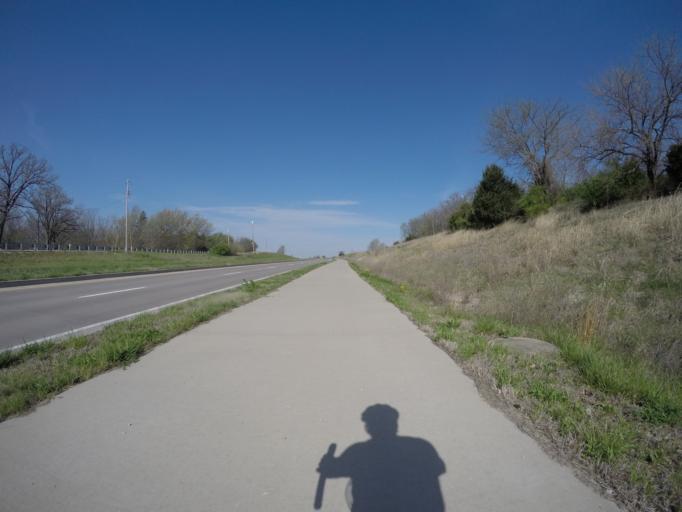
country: US
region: Missouri
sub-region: Cass County
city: Raymore
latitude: 38.8561
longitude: -94.4754
